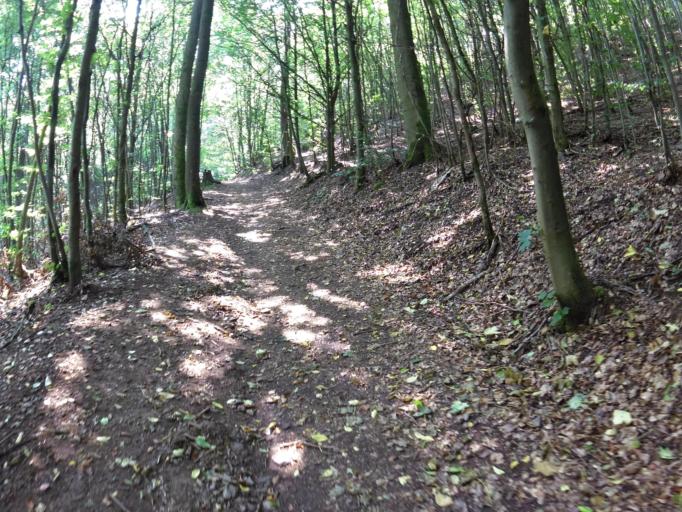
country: DE
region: Thuringia
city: Eisenach
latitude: 50.9469
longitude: 10.3257
